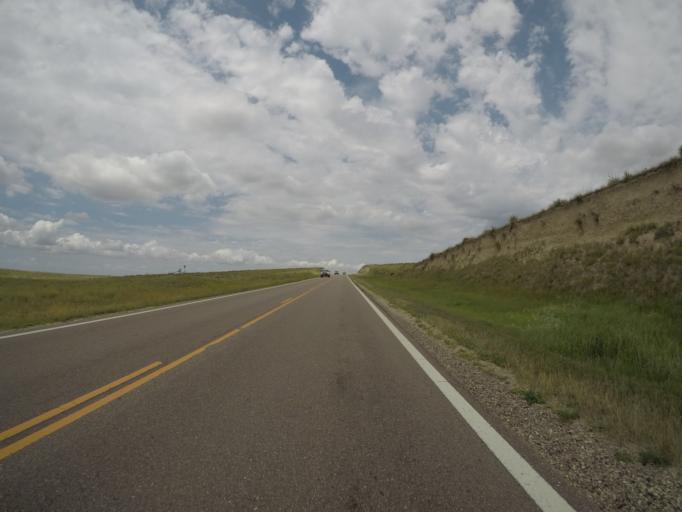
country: US
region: Kansas
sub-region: Rawlins County
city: Atwood
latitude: 39.7421
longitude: -101.0520
